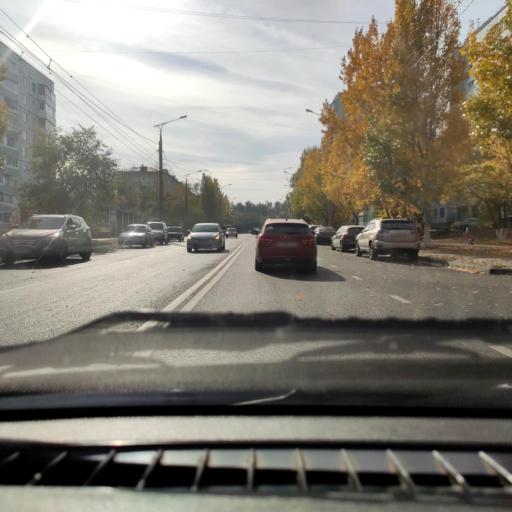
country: RU
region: Samara
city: Zhigulevsk
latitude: 53.4783
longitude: 49.4584
